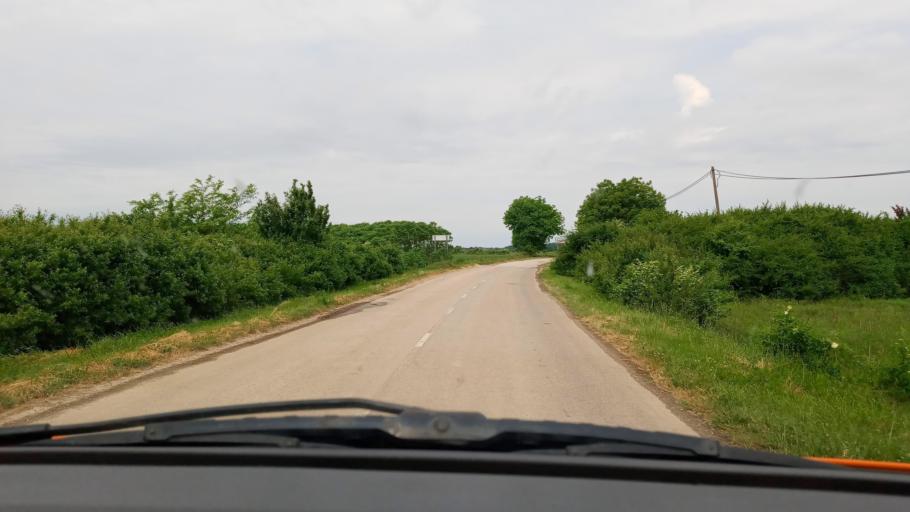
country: HU
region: Baranya
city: Vajszlo
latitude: 45.9092
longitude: 18.0293
